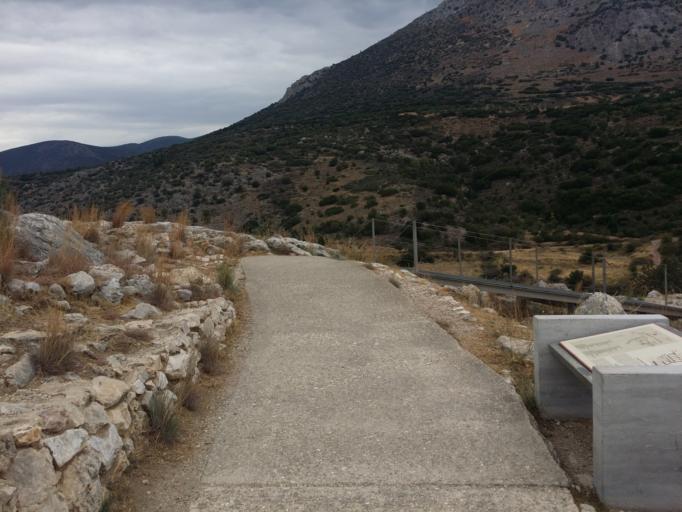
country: GR
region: Peloponnese
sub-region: Nomos Argolidos
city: Koutsopodi
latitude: 37.7304
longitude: 22.7584
